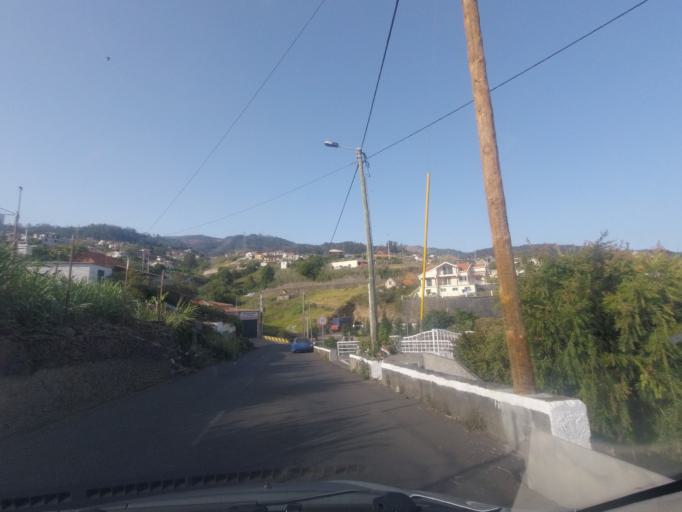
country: PT
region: Madeira
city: Ponta do Sol
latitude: 32.6964
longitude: -17.1123
